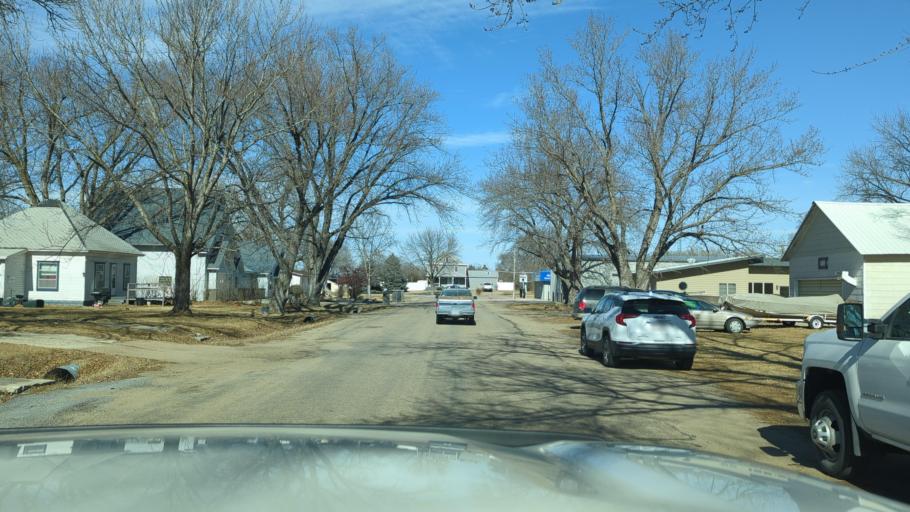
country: US
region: Nebraska
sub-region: Antelope County
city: Neligh
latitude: 42.2617
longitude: -98.3465
